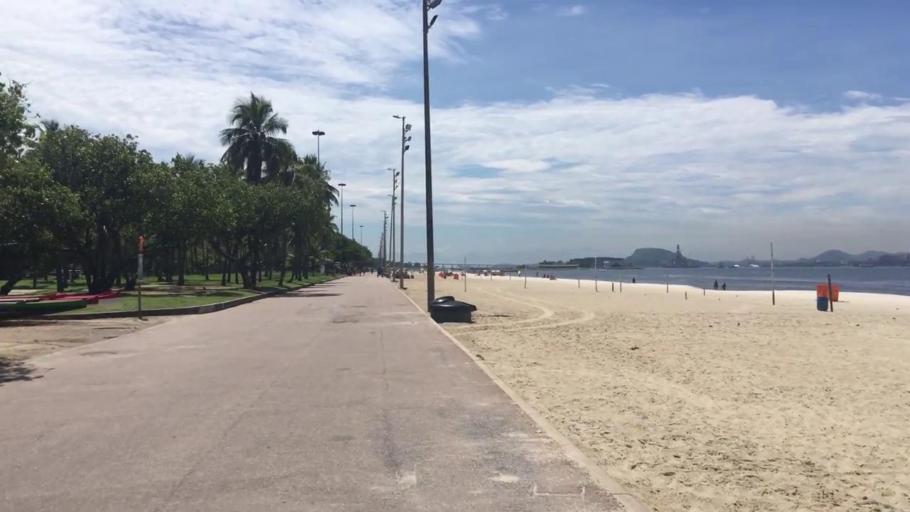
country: BR
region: Rio de Janeiro
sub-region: Rio De Janeiro
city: Rio de Janeiro
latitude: -22.9286
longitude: -43.1713
